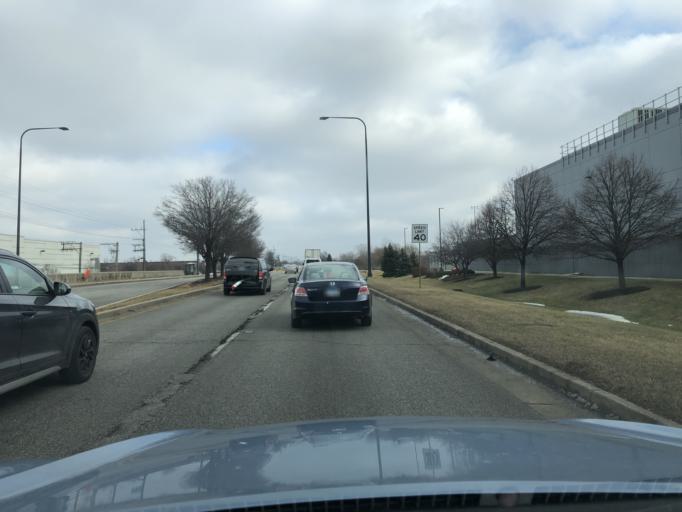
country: US
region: Illinois
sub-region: Cook County
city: Elk Grove Village
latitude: 41.9931
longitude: -87.9586
